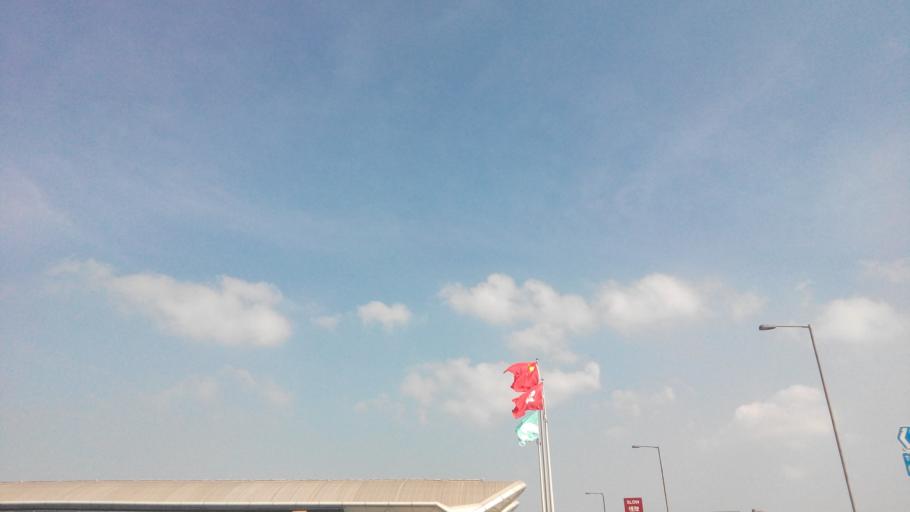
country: HK
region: Tuen Mun
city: Tuen Mun
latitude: 22.3135
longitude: 113.9370
